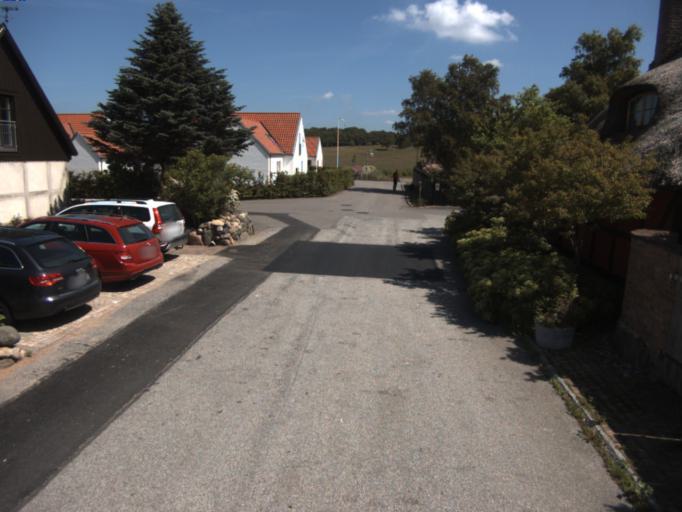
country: DK
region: Capital Region
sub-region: Helsingor Kommune
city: Hellebaek
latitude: 56.1224
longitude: 12.6032
